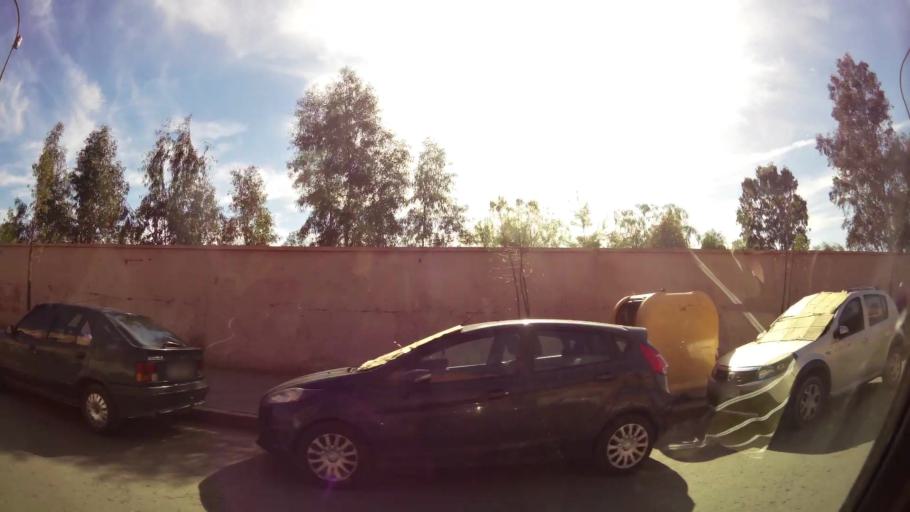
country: MA
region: Marrakech-Tensift-Al Haouz
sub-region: Marrakech
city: Marrakesh
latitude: 31.6066
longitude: -7.9636
